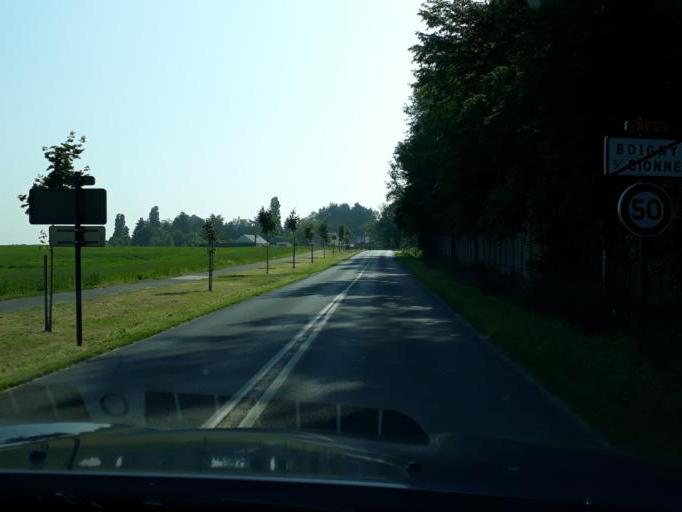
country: FR
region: Centre
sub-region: Departement du Loiret
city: Boigny-sur-Bionne
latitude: 47.9218
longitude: 2.0204
